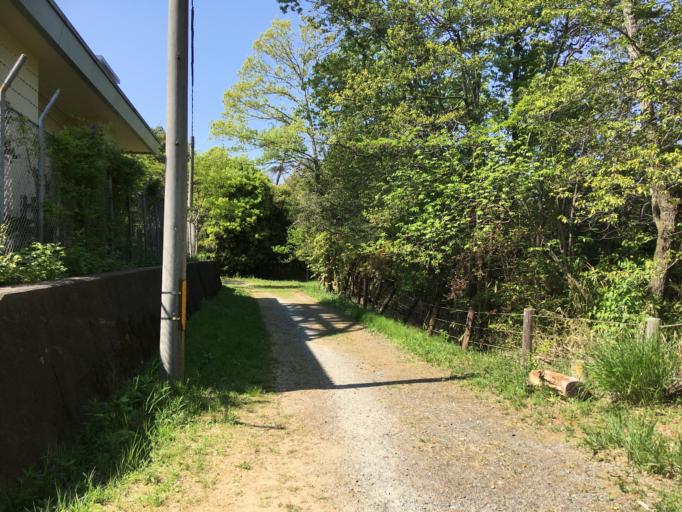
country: JP
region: Nara
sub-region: Ikoma-shi
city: Ikoma
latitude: 34.6891
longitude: 135.7179
